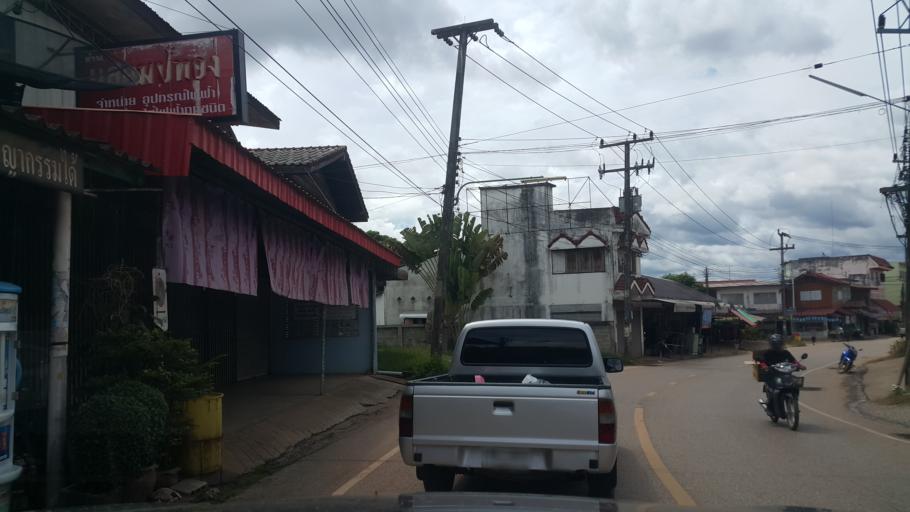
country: TH
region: Phitsanulok
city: Chat Trakan
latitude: 17.2749
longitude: 100.6047
